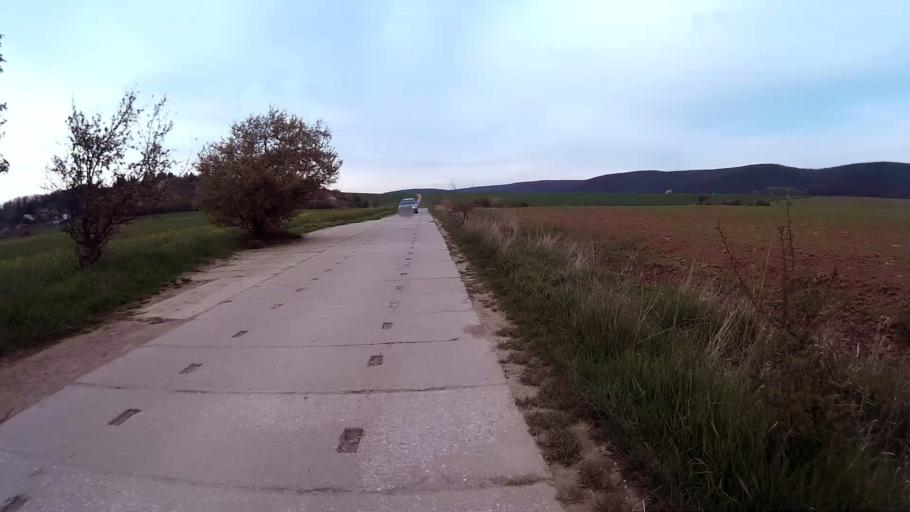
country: CZ
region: South Moravian
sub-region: Mesto Brno
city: Mokra Hora
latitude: 49.2392
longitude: 16.5458
